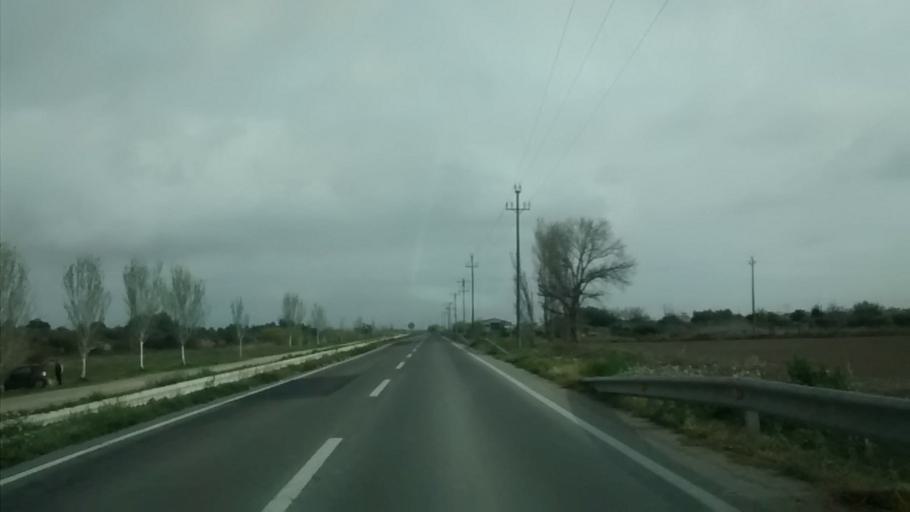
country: ES
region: Catalonia
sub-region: Provincia de Tarragona
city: Sant Carles de la Rapita
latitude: 40.6268
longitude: 0.6002
